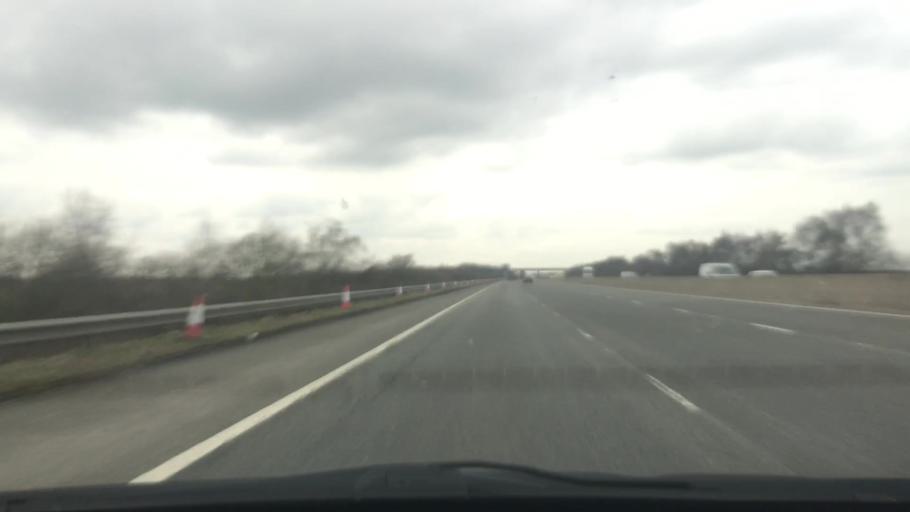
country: GB
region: England
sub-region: Doncaster
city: Hatfield
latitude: 53.5742
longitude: -0.9132
